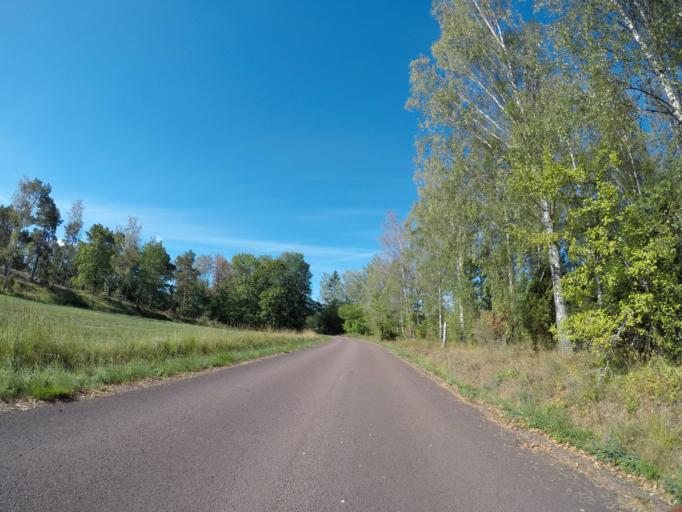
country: AX
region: Alands landsbygd
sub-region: Finstroem
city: Finstroem
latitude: 60.2991
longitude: 19.8819
